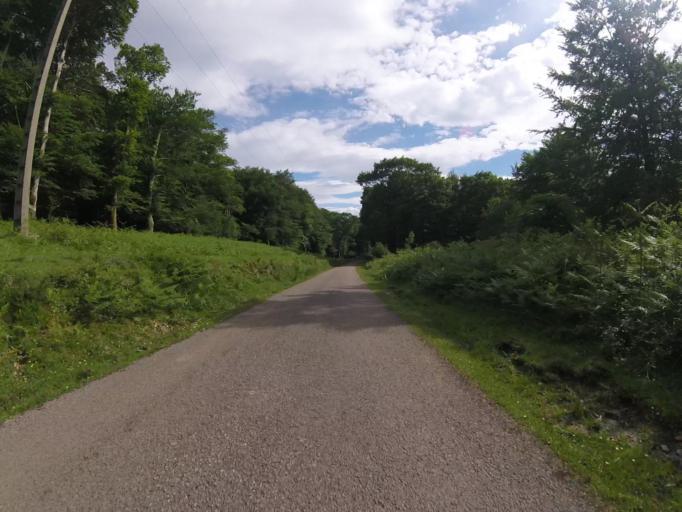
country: ES
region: Navarre
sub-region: Provincia de Navarra
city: Arantza
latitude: 43.2373
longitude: -1.8038
